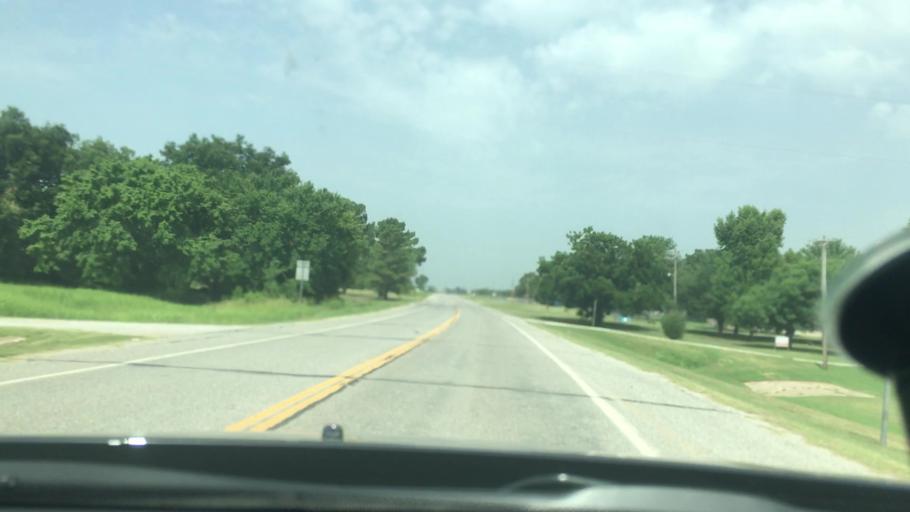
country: US
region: Oklahoma
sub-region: Garvin County
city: Pauls Valley
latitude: 34.8262
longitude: -97.2639
